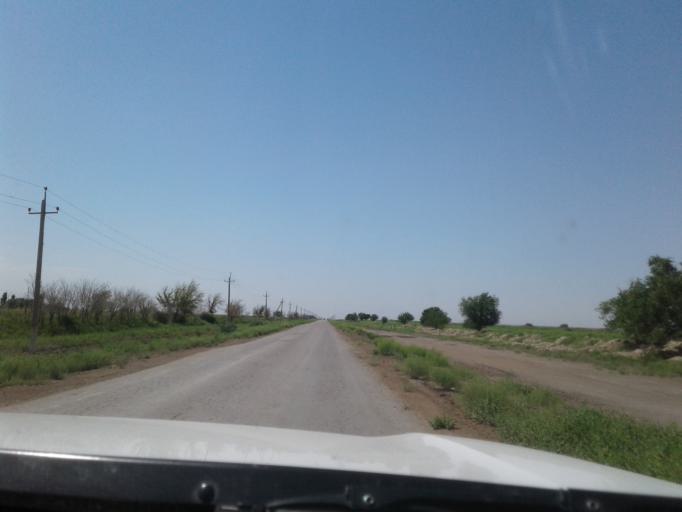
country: TM
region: Dasoguz
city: Koeneuergench
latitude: 41.8525
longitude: 58.7051
